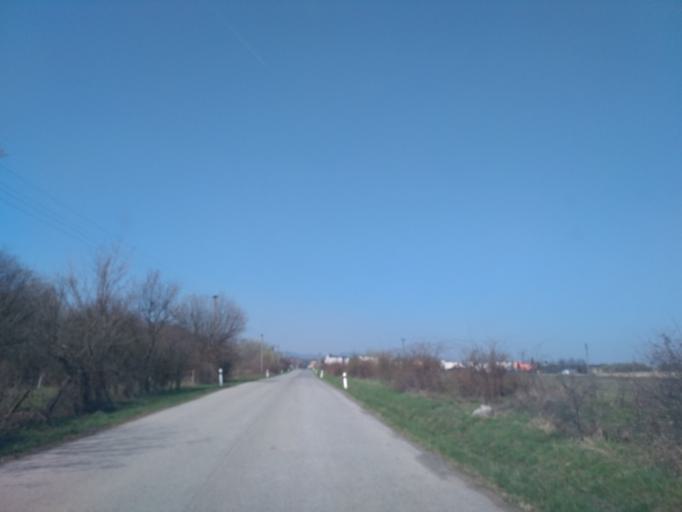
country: SK
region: Presovsky
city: Vranov nad Topl'ou
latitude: 48.8004
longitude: 21.6543
